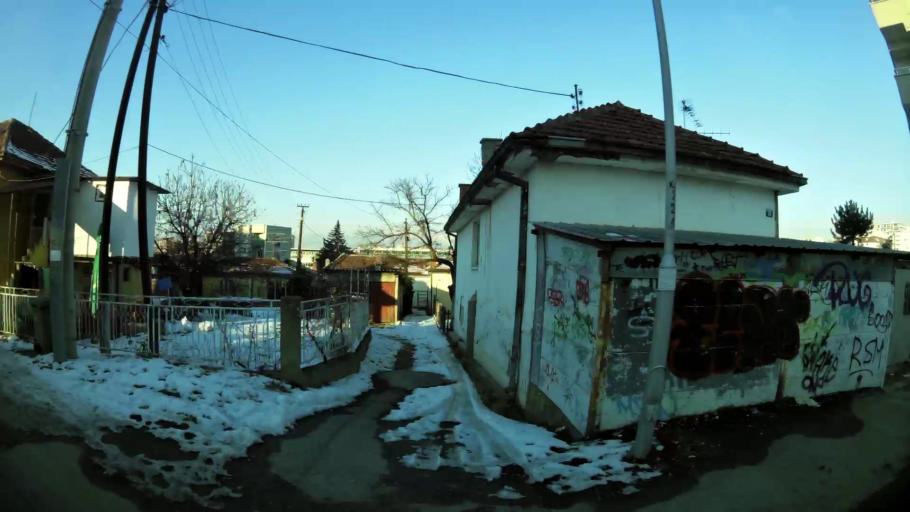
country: MK
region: Karpos
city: Skopje
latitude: 41.9971
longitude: 21.3935
